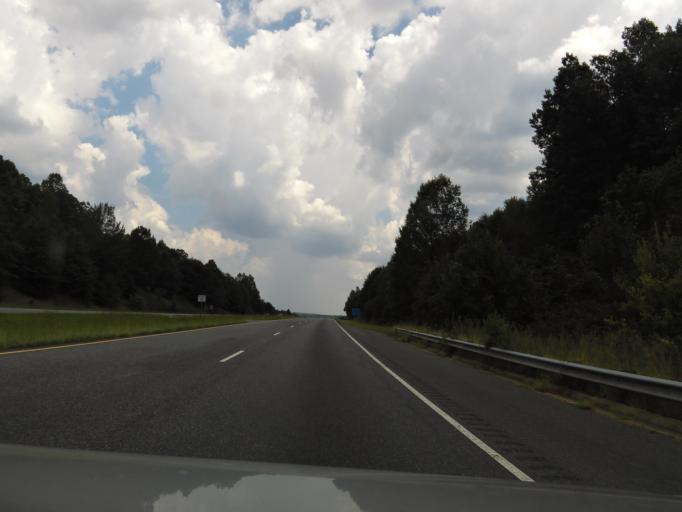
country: US
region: North Carolina
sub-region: Rutherford County
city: Rutherfordton
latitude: 35.2908
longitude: -82.0169
